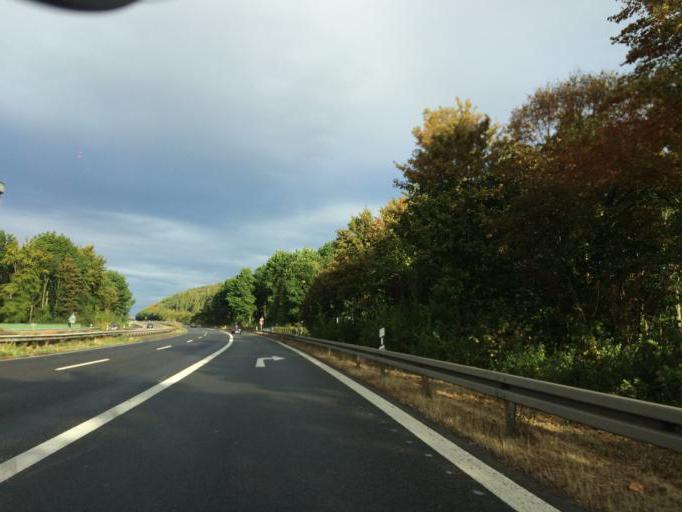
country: DE
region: North Rhine-Westphalia
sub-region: Regierungsbezirk Koln
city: Konigswinter
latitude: 50.7243
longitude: 7.1642
